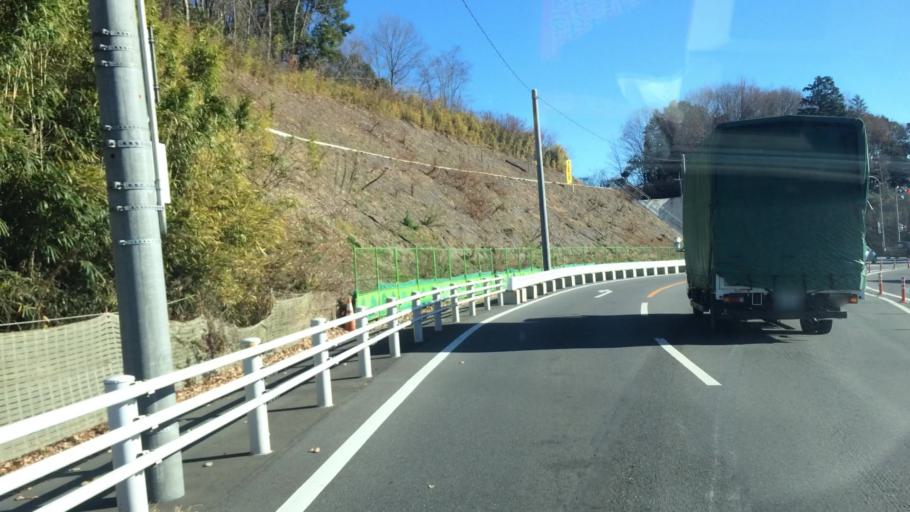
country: JP
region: Tochigi
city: Utsunomiya-shi
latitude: 36.5937
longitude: 139.8676
